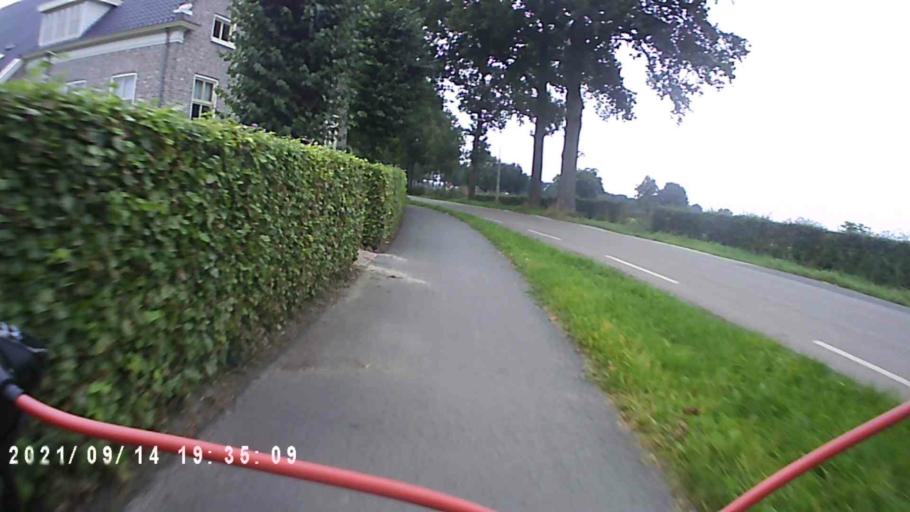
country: NL
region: Drenthe
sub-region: Gemeente Tynaarlo
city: Zuidlaren
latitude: 53.1246
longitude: 6.6655
